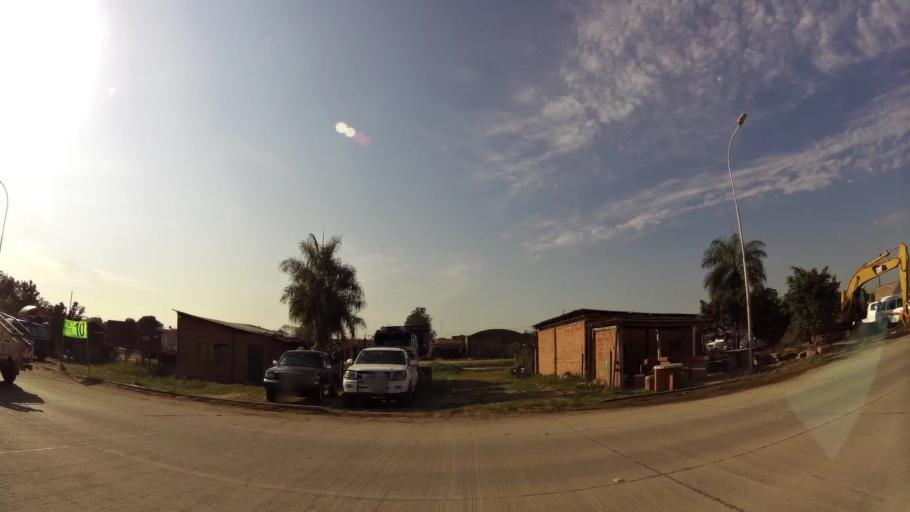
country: BO
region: Santa Cruz
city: Santa Cruz de la Sierra
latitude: -17.7261
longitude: -63.1349
